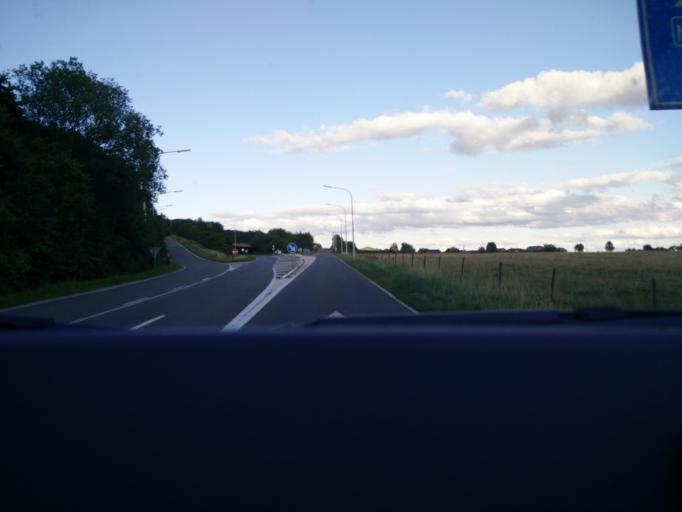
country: BE
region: Wallonia
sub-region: Province de Namur
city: Onhaye
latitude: 50.2420
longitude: 4.8232
